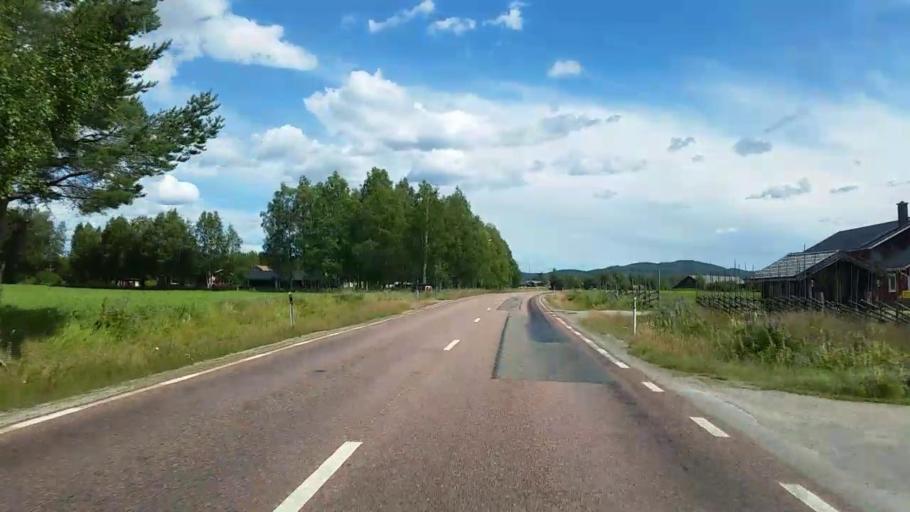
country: SE
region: Gaevleborg
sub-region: Ovanakers Kommun
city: Edsbyn
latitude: 61.3468
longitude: 15.6168
